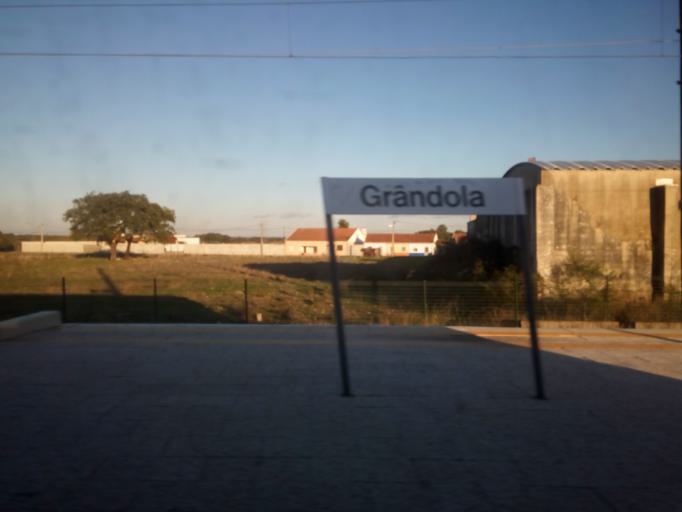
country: PT
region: Setubal
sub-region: Grandola
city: Grandola
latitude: 38.1833
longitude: -8.5548
